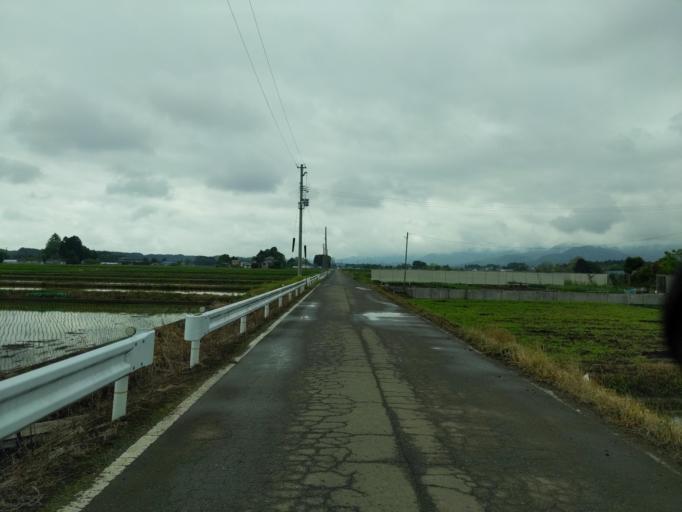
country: JP
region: Fukushima
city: Koriyama
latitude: 37.3556
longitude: 140.3112
